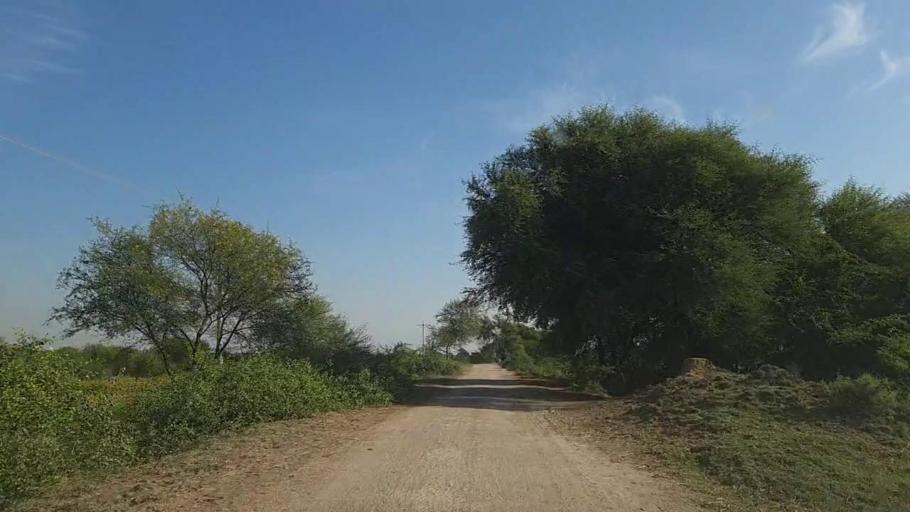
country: PK
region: Sindh
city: Bulri
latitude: 24.7839
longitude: 68.3514
